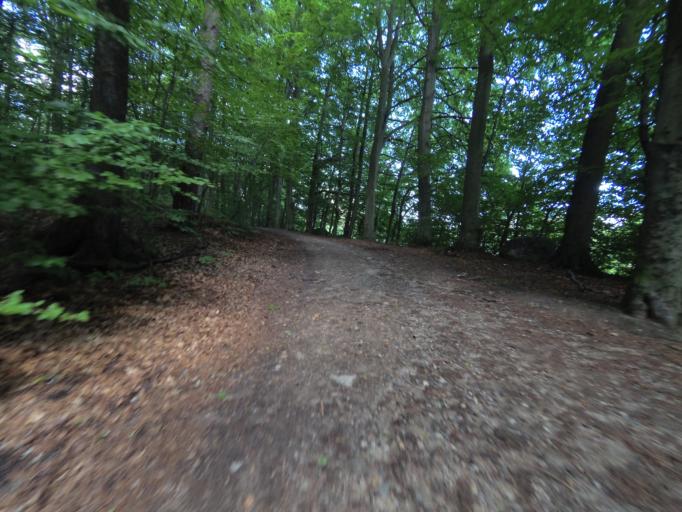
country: PL
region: Pomeranian Voivodeship
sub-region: Gdynia
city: Wielki Kack
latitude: 54.4914
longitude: 18.5061
